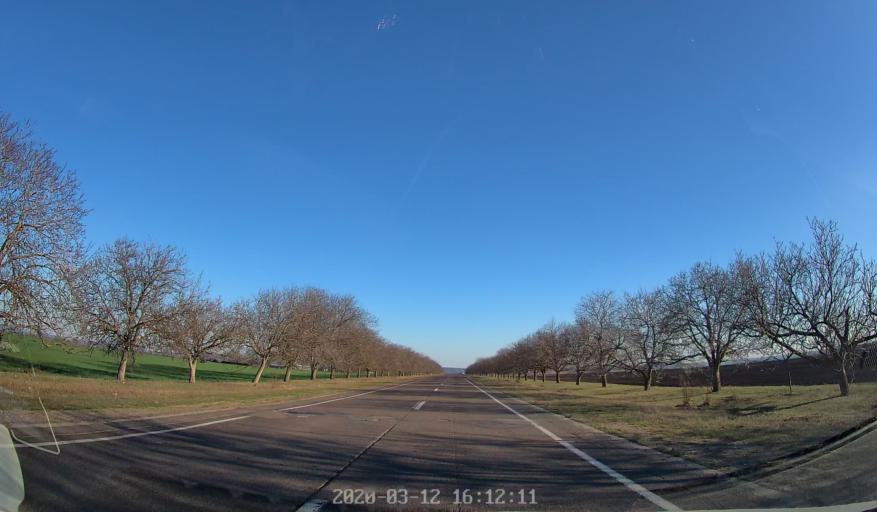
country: MD
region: Anenii Noi
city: Anenii Noi
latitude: 46.9386
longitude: 29.2693
